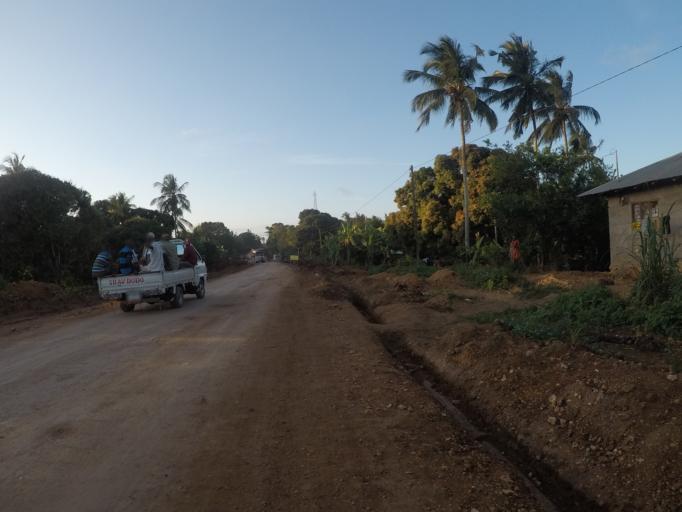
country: TZ
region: Zanzibar North
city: Gamba
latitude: -5.9207
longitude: 39.2999
